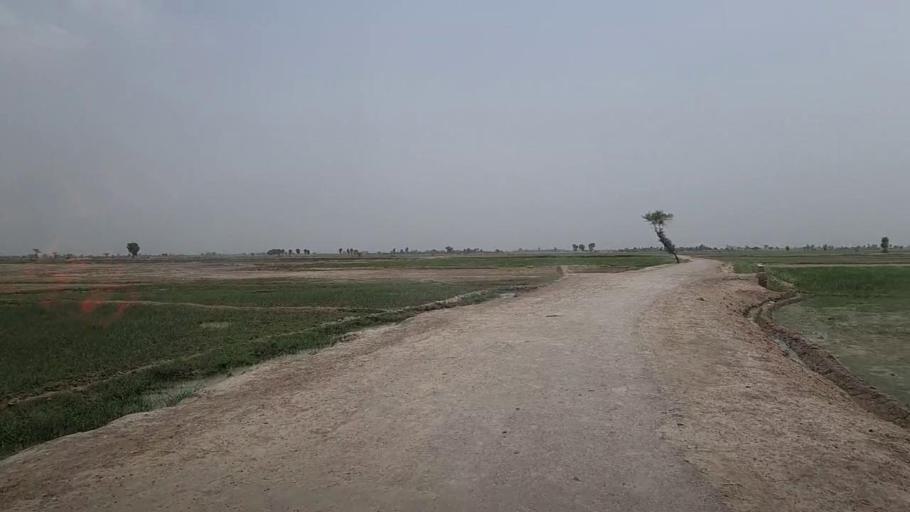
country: PK
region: Sindh
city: Sita Road
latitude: 27.0707
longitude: 67.8528
